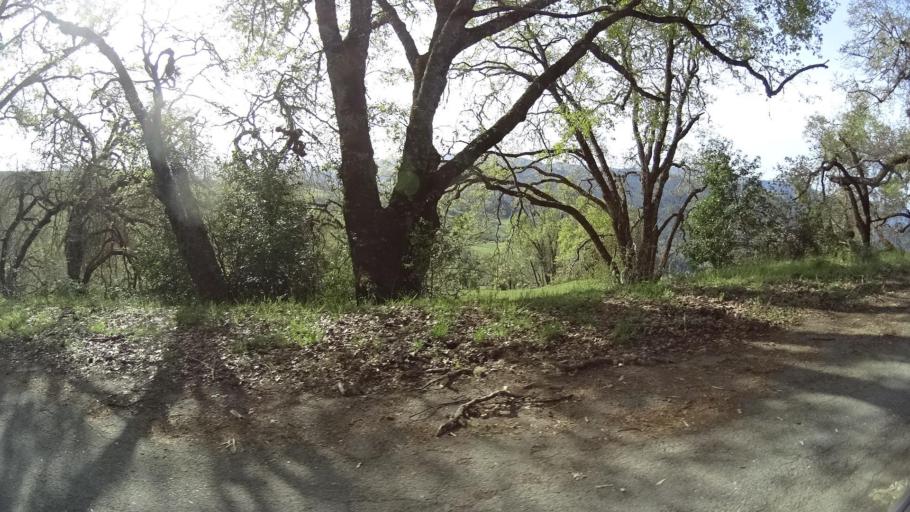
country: US
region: California
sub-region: Humboldt County
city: Hydesville
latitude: 40.6386
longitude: -123.8940
